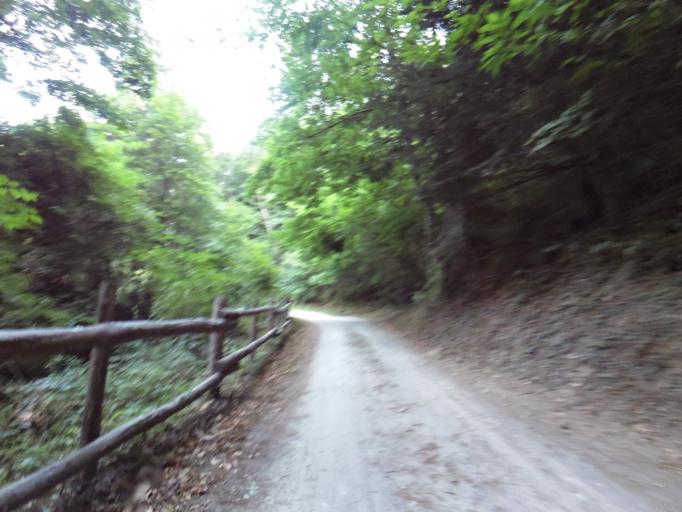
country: IT
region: Calabria
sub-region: Provincia di Vibo-Valentia
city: Mongiana
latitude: 38.5160
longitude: 16.3132
